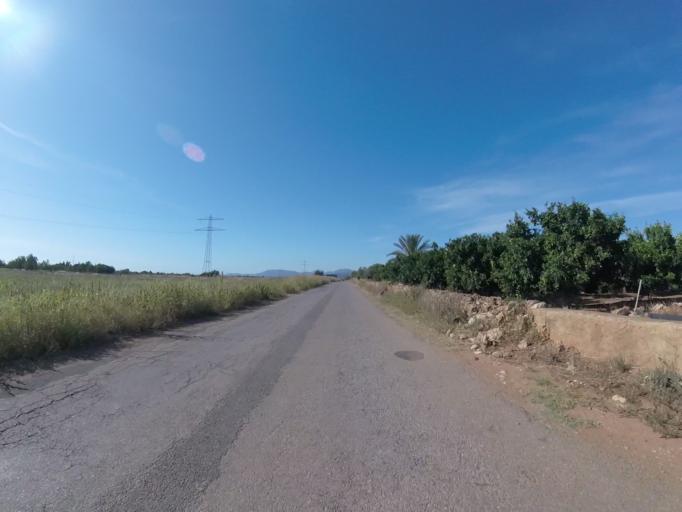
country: ES
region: Valencia
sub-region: Provincia de Castello
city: Torreblanca
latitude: 40.2162
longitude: 0.2179
